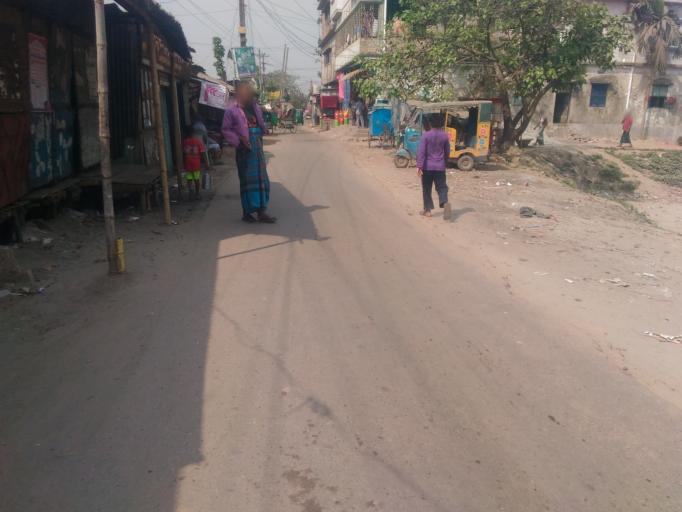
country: BD
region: Dhaka
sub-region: Dhaka
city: Dhaka
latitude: 23.6695
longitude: 90.4194
